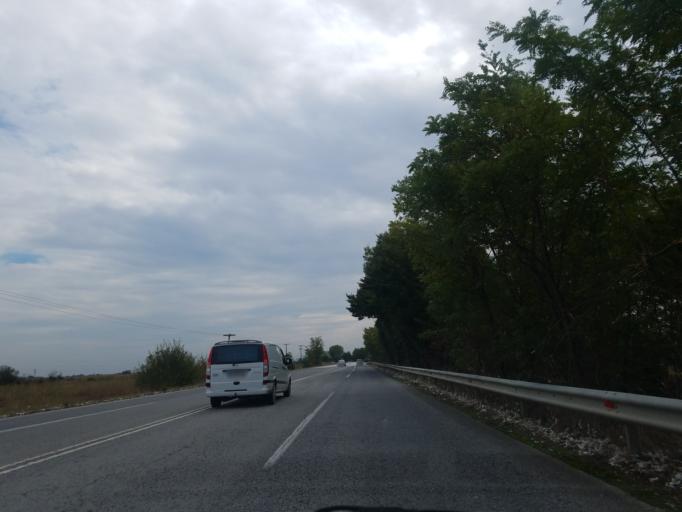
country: GR
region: Thessaly
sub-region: Nomos Kardhitsas
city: Karpochori
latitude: 39.3583
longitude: 22.0454
